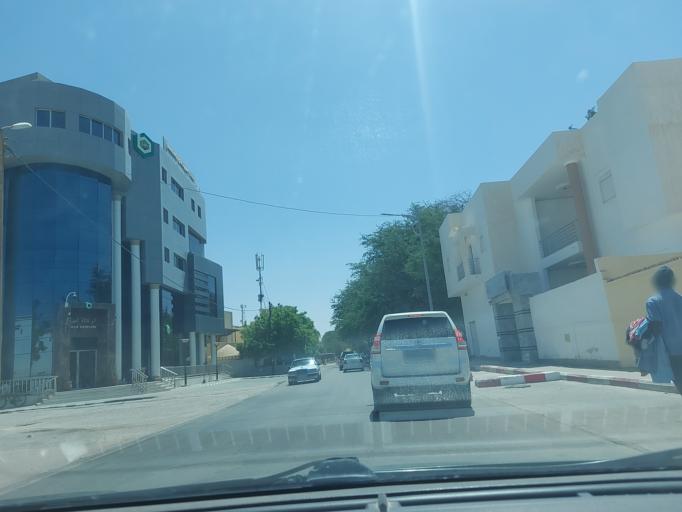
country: MR
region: Nouakchott
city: Nouakchott
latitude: 18.0951
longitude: -15.9775
